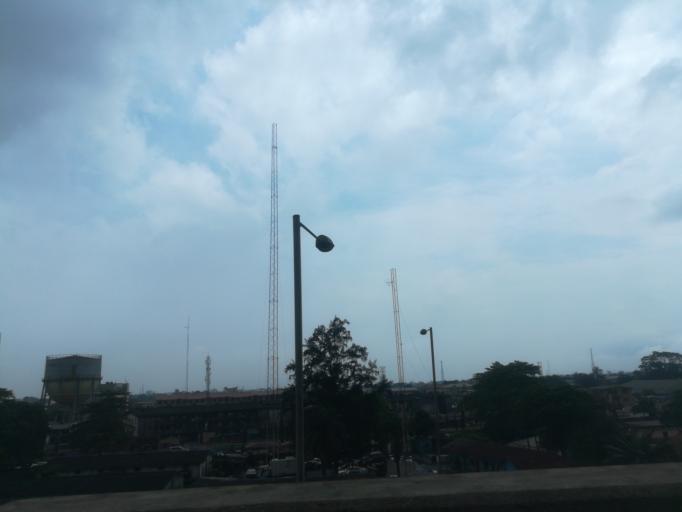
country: NG
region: Lagos
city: Surulere
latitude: 6.4835
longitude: 3.3659
